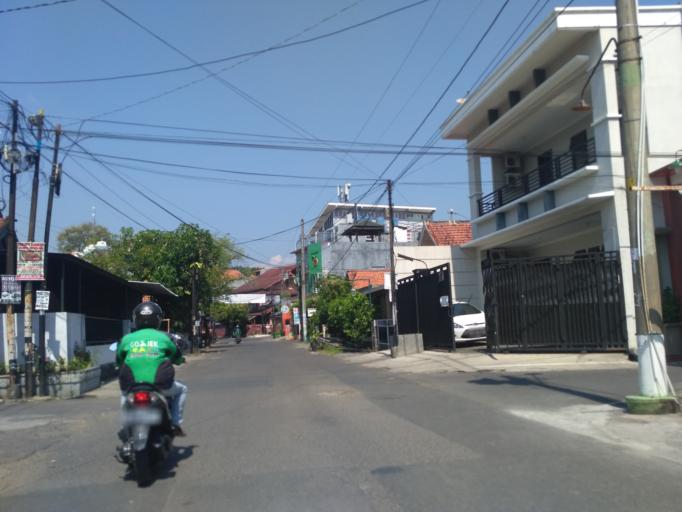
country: ID
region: Central Java
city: Semarang
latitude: -6.9994
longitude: 110.4258
